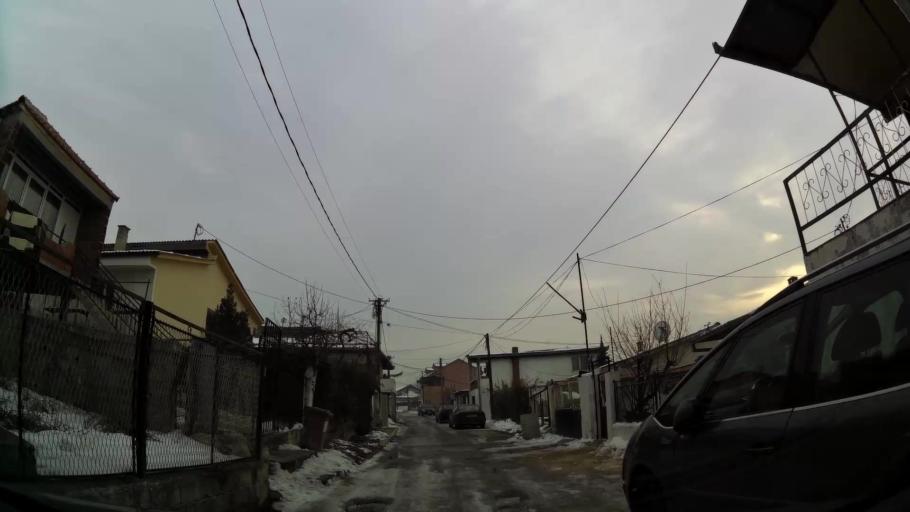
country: MK
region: Suto Orizari
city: Suto Orizare
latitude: 42.0373
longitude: 21.4274
